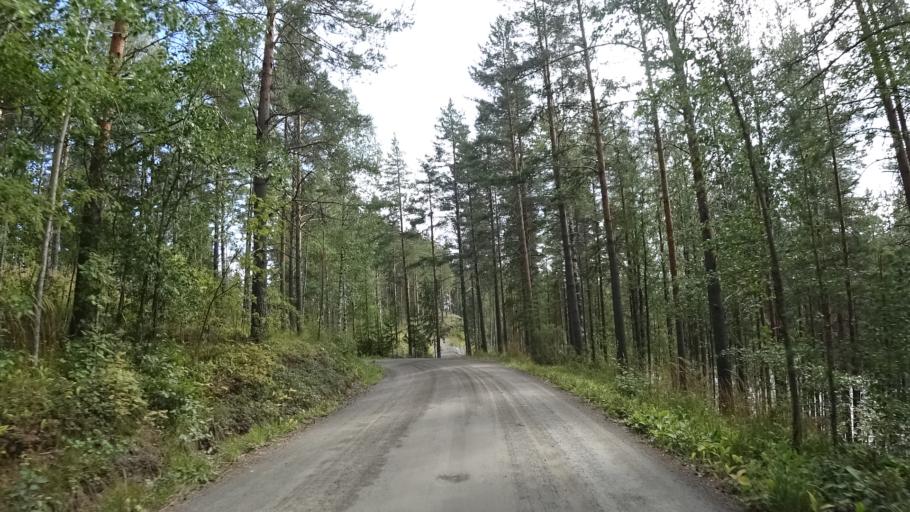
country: FI
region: North Karelia
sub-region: Joensuu
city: Pyhaeselkae
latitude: 62.3744
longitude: 29.8176
